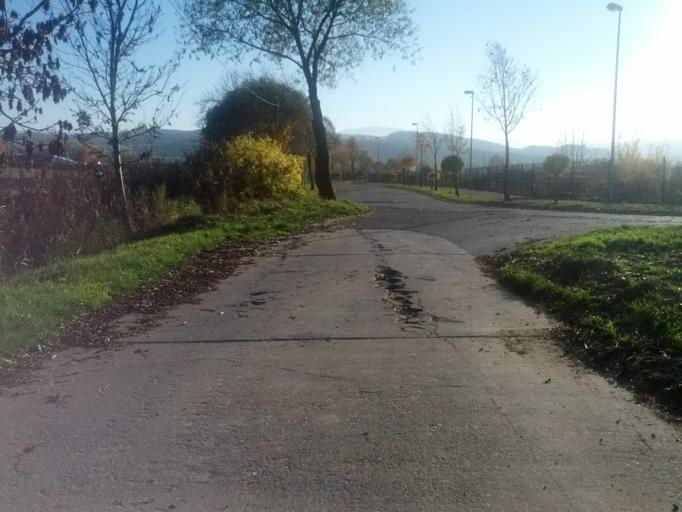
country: DE
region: Thuringia
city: Mechterstadt
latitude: 50.9488
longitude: 10.4990
